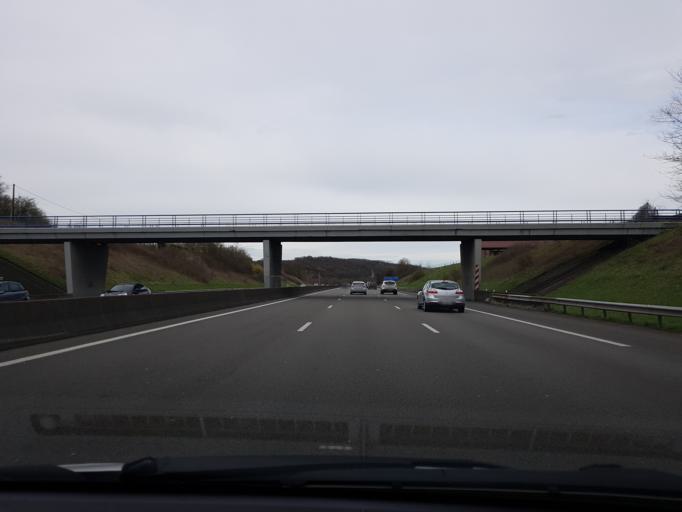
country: FR
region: Bourgogne
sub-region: Departement de Saone-et-Loire
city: Saint-Martin-Belle-Roche
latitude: 46.3967
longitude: 4.8543
